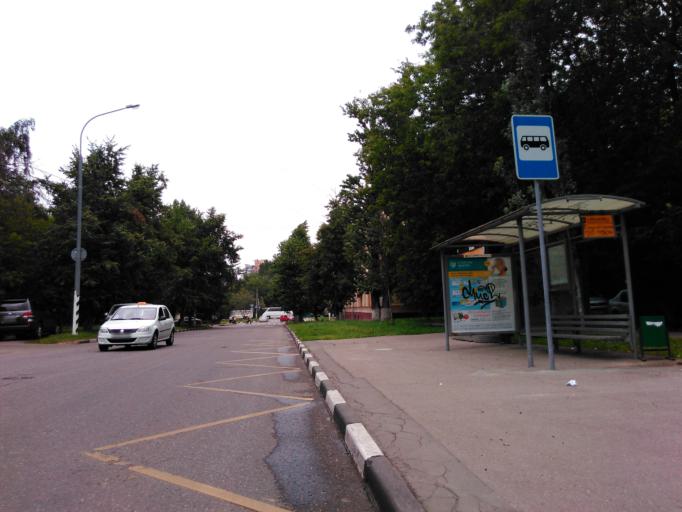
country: RU
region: Moskovskaya
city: Leninskiye Gory
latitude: 55.6890
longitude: 37.5655
